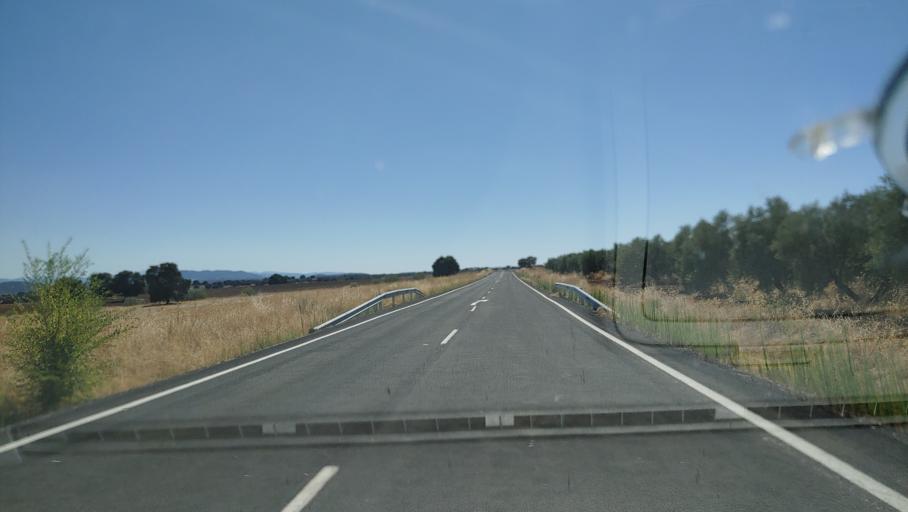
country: ES
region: Castille-La Mancha
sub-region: Provincia de Ciudad Real
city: Albaladejo
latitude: 38.5503
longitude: -2.7828
